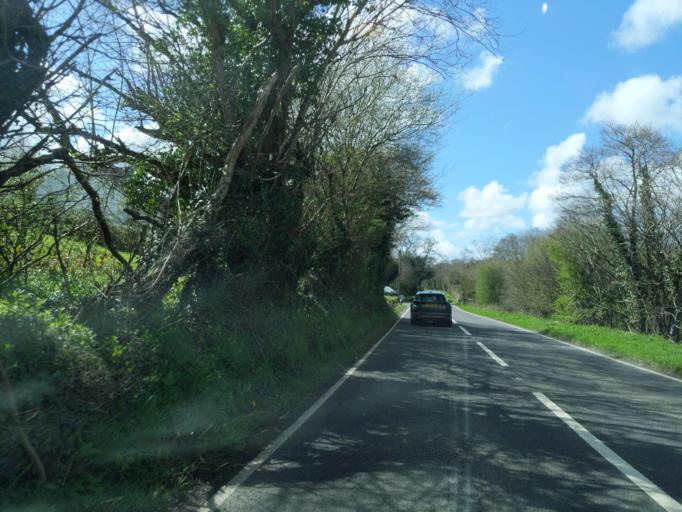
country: GB
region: England
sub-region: Cornwall
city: Wadebridge
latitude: 50.5078
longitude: -4.7941
